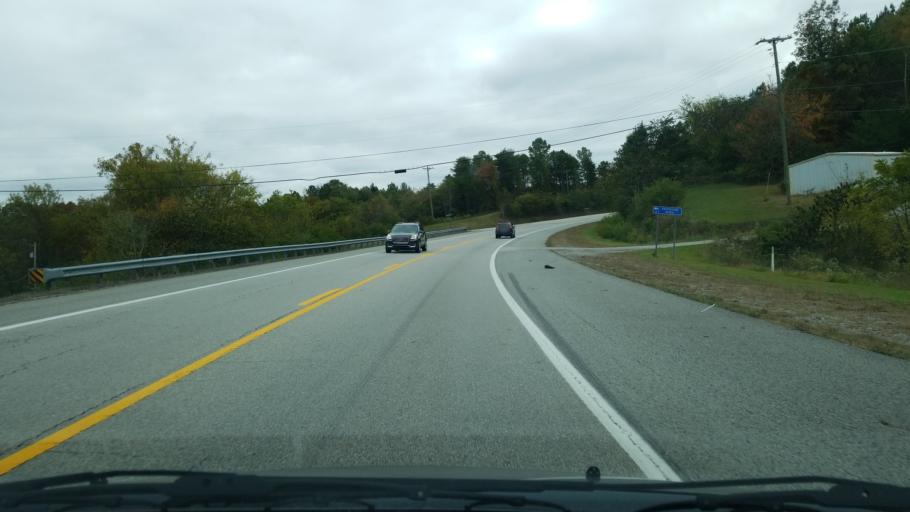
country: US
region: Tennessee
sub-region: Rhea County
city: Dayton
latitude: 35.4562
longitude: -85.0106
